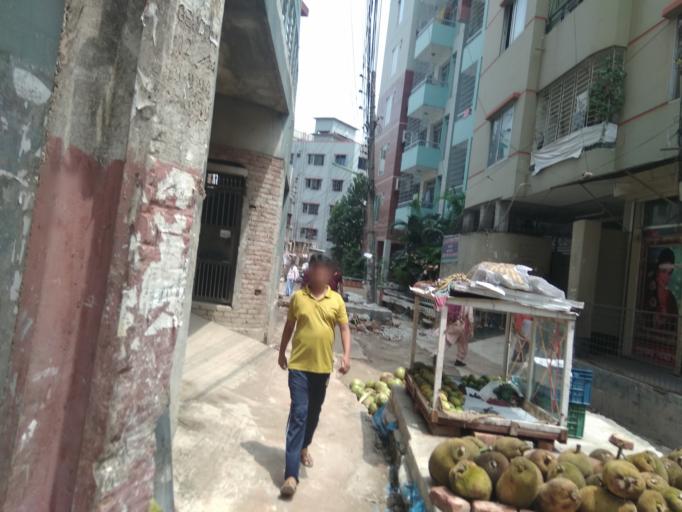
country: BD
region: Dhaka
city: Azimpur
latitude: 23.8028
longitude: 90.3668
